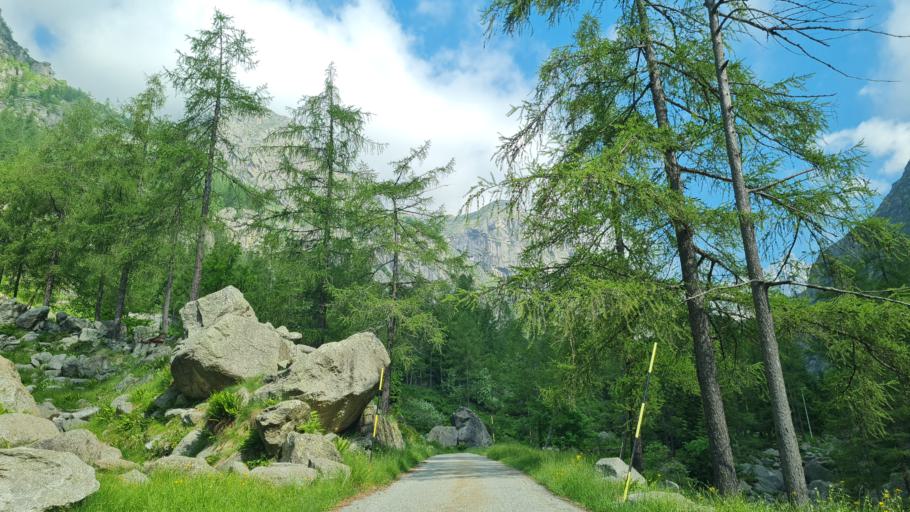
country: IT
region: Piedmont
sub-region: Provincia di Torino
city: Noasca
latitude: 45.4630
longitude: 7.3779
